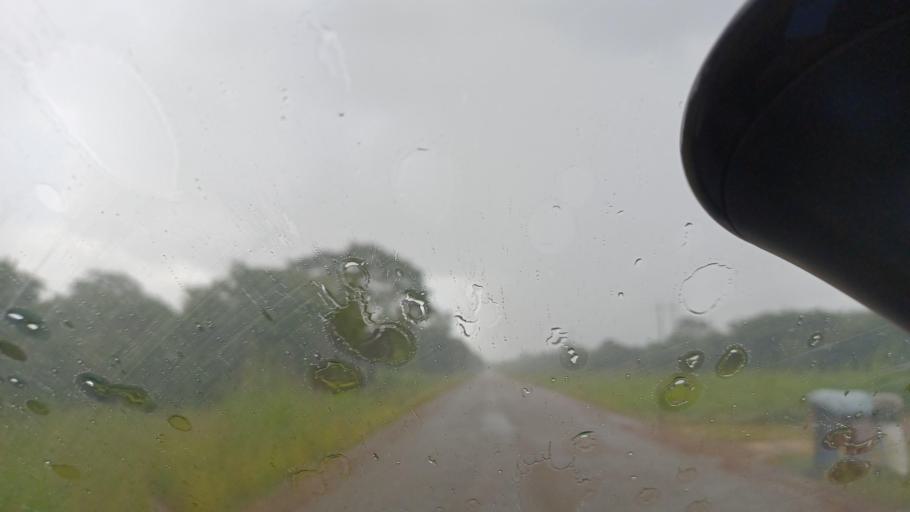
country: ZM
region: North-Western
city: Kasempa
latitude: -13.0907
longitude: 25.9443
